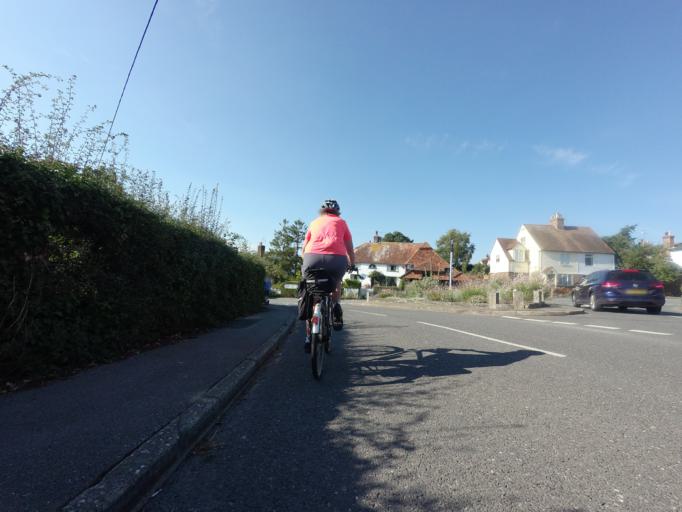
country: GB
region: England
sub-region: Kent
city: Tenterden
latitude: 51.0137
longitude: 0.7079
